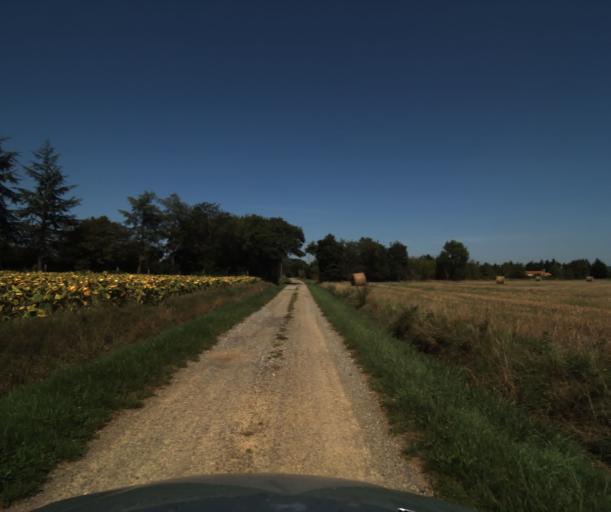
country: FR
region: Midi-Pyrenees
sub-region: Departement de la Haute-Garonne
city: Lacasse
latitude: 43.4353
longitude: 1.2827
